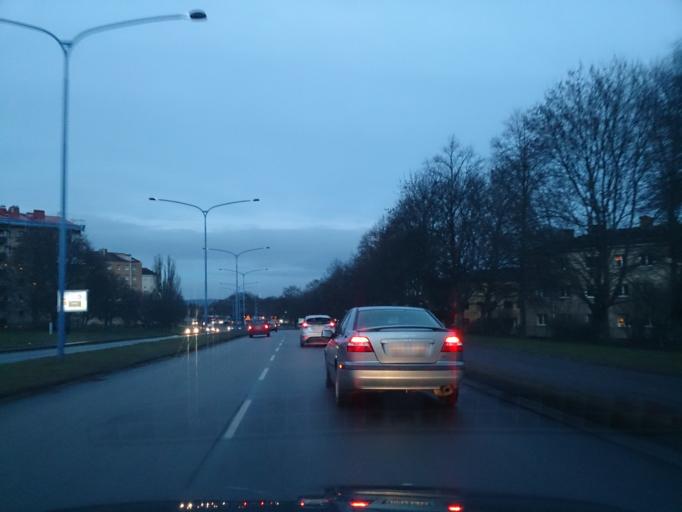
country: SE
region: OEstergoetland
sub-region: Norrkopings Kommun
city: Norrkoping
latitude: 58.6000
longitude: 16.1638
